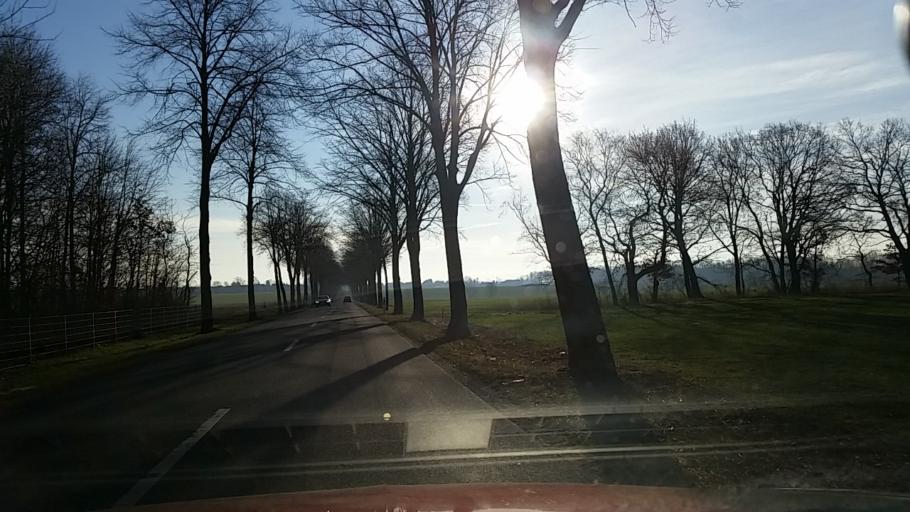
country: DE
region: Lower Saxony
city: Ruhen
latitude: 52.4830
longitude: 10.8526
